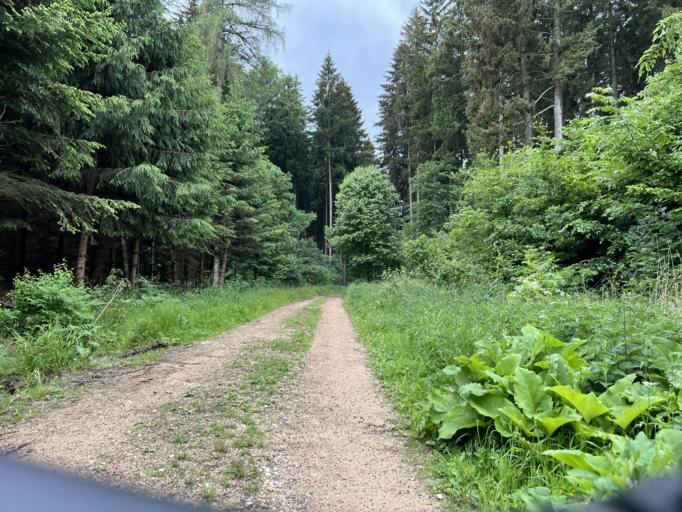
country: DE
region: Baden-Wuerttemberg
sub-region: Tuebingen Region
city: Sigmaringen
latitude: 48.1014
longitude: 9.2479
